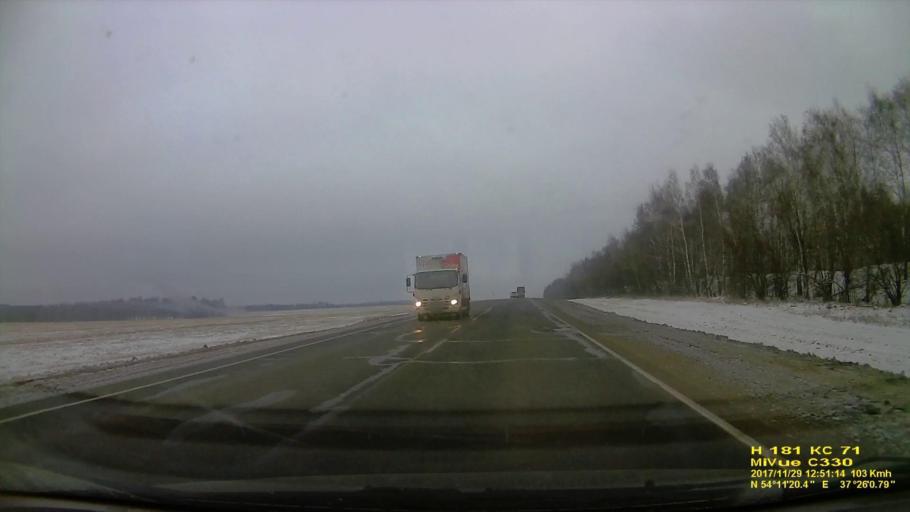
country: RU
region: Tula
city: Barsuki
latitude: 54.1890
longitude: 37.4336
